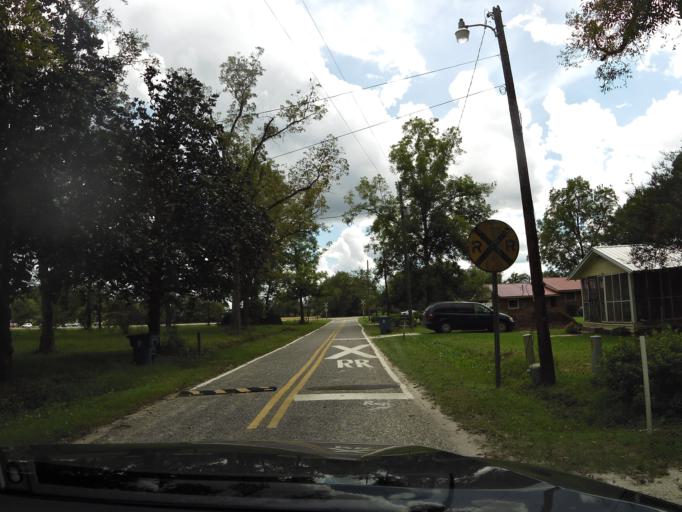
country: US
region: Georgia
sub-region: Brantley County
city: Nahunta
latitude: 31.2033
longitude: -81.9963
